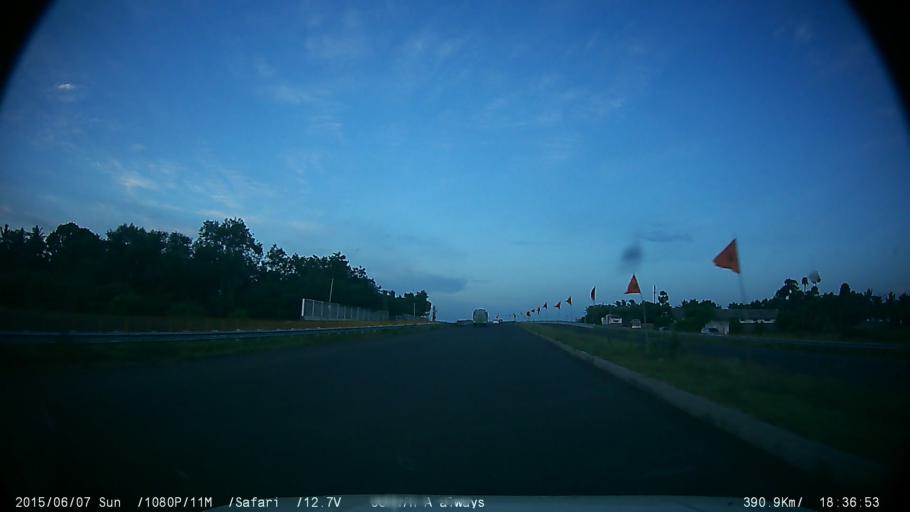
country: IN
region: Tamil Nadu
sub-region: Tiruppur
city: Avinashi
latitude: 11.1990
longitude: 77.3094
